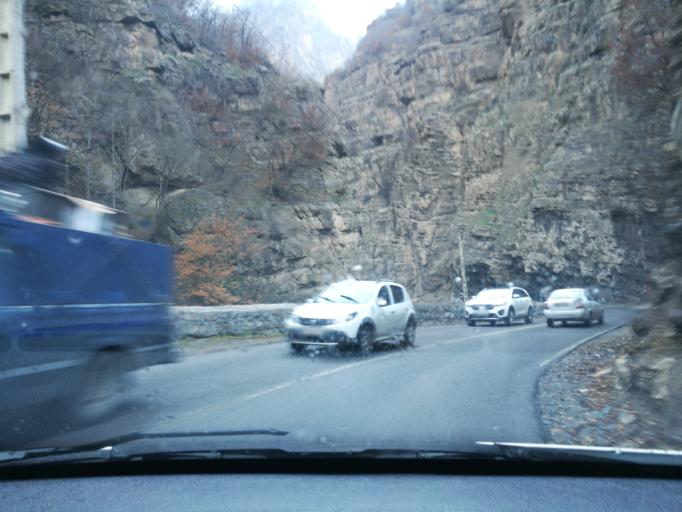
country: IR
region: Mazandaran
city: Chalus
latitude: 36.2704
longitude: 51.2477
